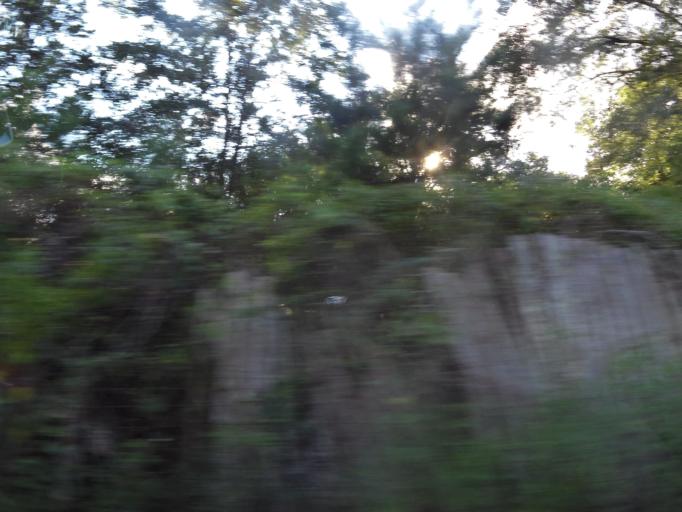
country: US
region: Georgia
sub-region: Lowndes County
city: Valdosta
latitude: 30.8222
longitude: -83.3004
